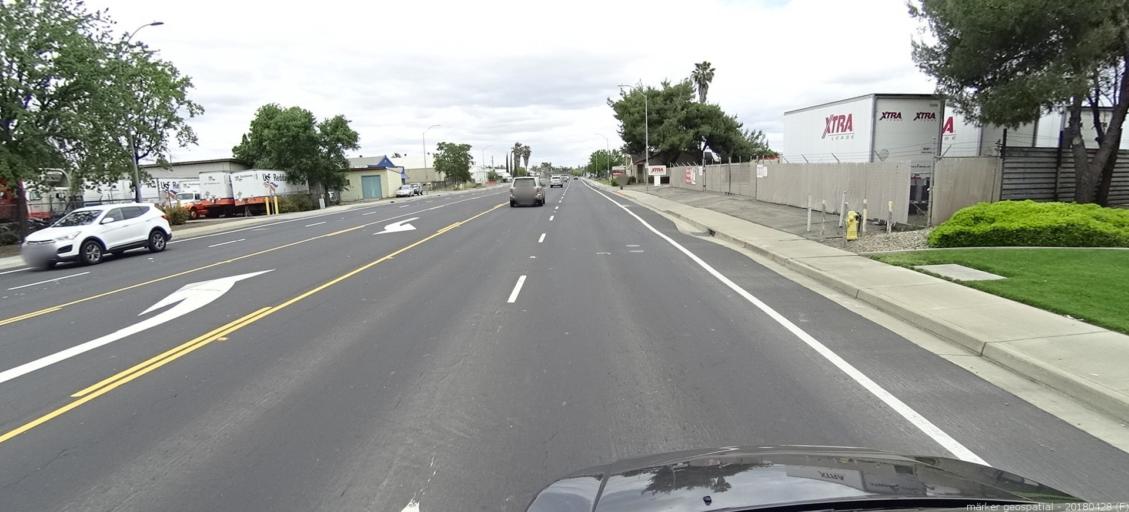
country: US
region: California
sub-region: Yolo County
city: West Sacramento
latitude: 38.5818
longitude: -121.5481
